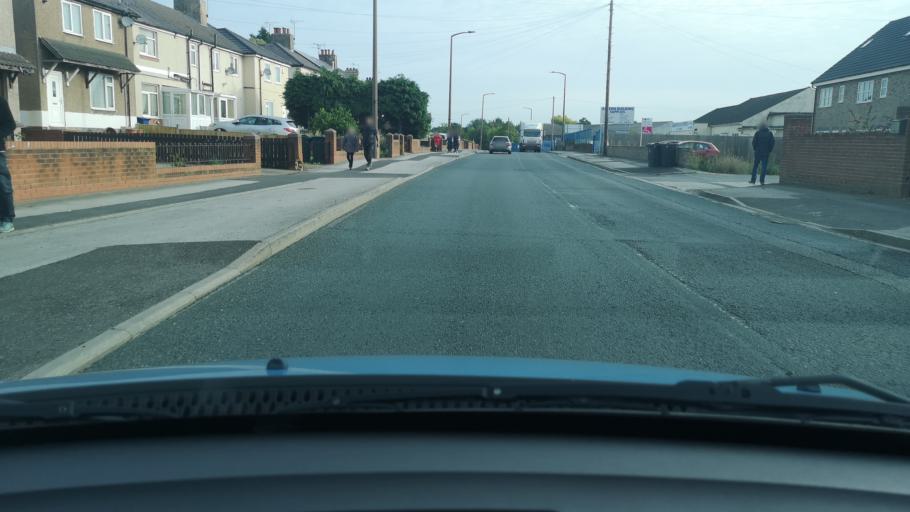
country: GB
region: England
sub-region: Doncaster
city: Askern
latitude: 53.6108
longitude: -1.1539
